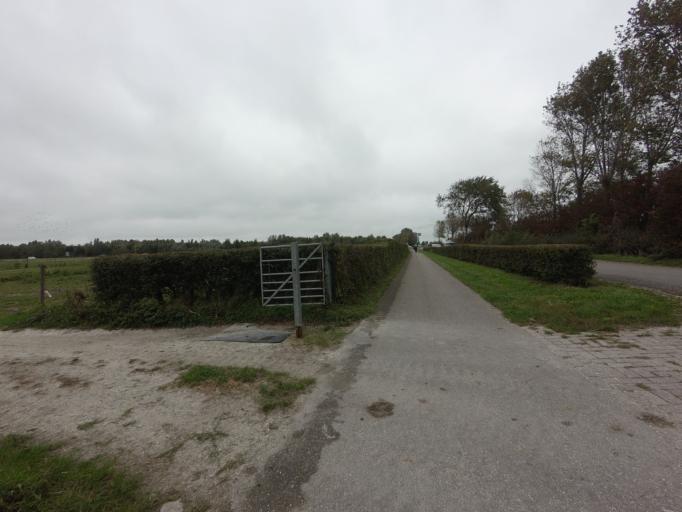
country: NL
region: Zeeland
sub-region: Gemeente Vlissingen
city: Vlissingen
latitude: 51.4865
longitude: 3.5561
